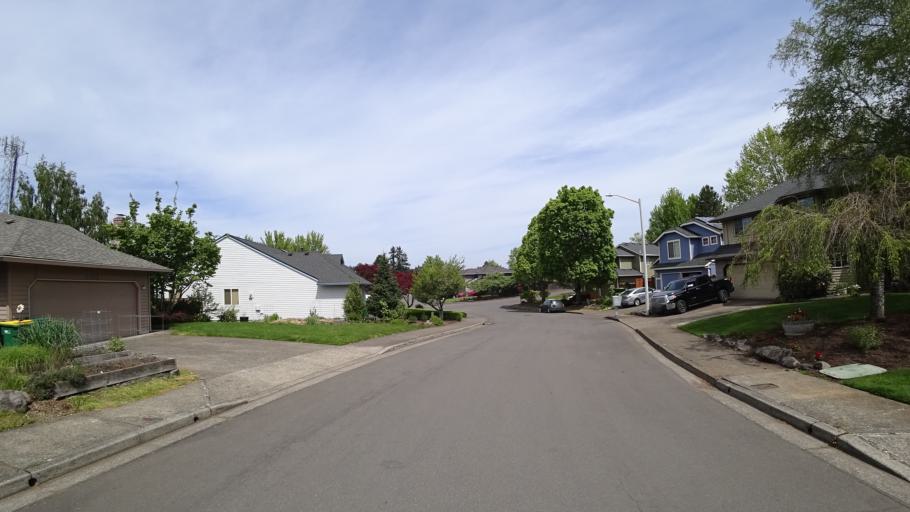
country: US
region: Oregon
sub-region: Washington County
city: Aloha
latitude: 45.4597
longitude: -122.8402
